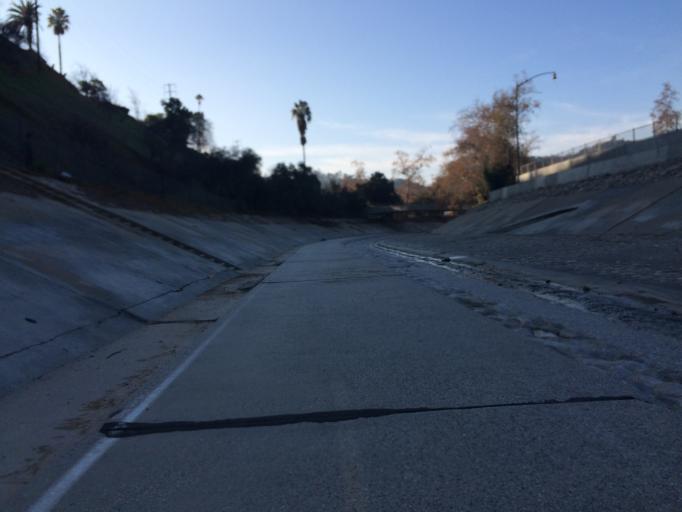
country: US
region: California
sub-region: Los Angeles County
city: South Pasadena
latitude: 34.1095
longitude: -118.1845
